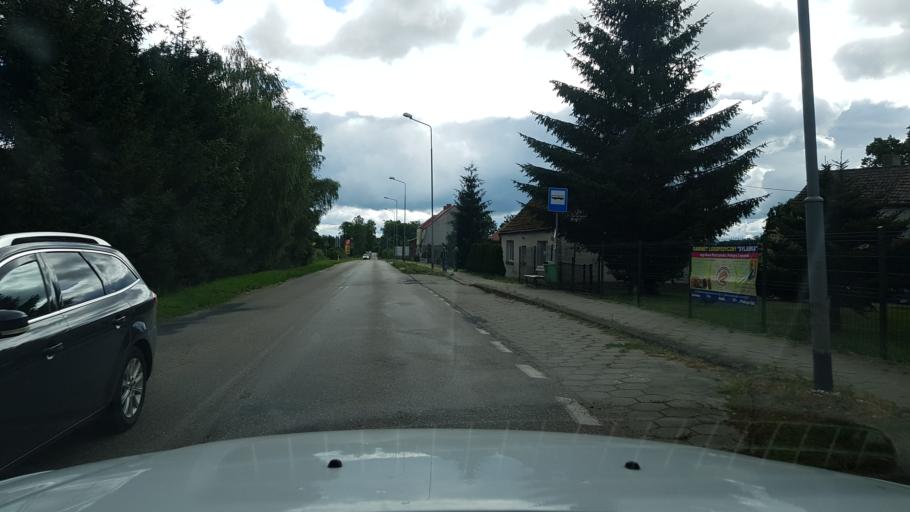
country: PL
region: West Pomeranian Voivodeship
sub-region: Powiat swidwinski
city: Rabino
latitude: 53.7746
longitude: 15.9678
